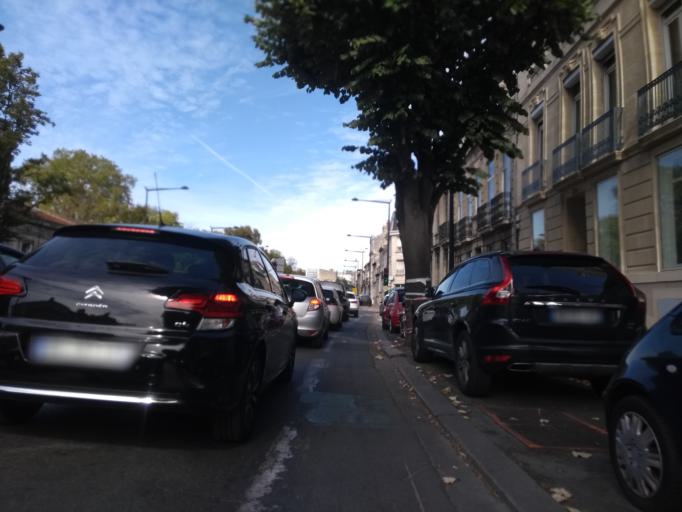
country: FR
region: Aquitaine
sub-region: Departement de la Gironde
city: Bordeaux
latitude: 44.8462
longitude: -0.5983
